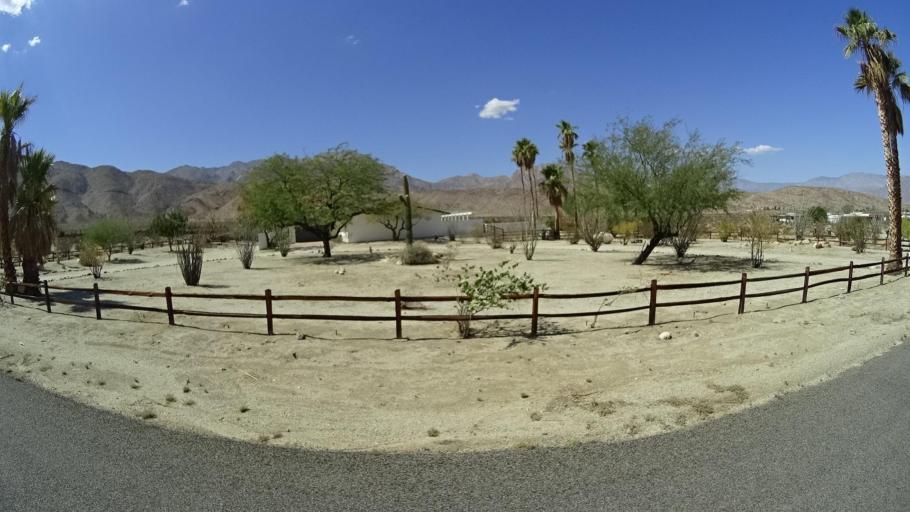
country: US
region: California
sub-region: San Diego County
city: Borrego Springs
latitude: 33.2306
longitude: -116.3893
